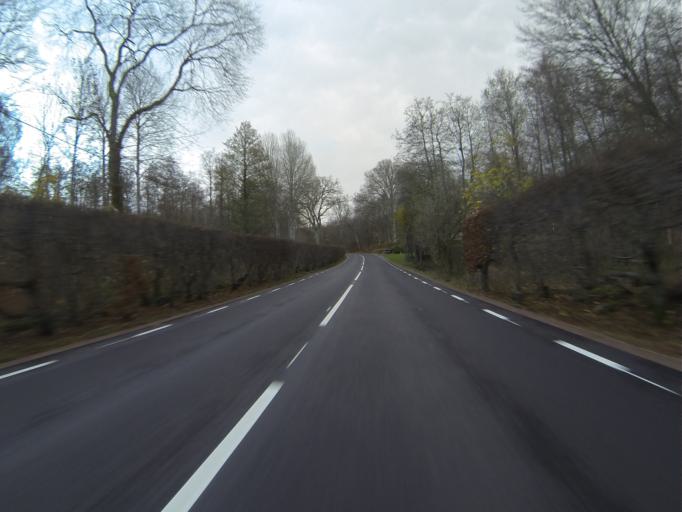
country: SE
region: Skane
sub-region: Lunds Kommun
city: Genarp
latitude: 55.5884
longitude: 13.4197
